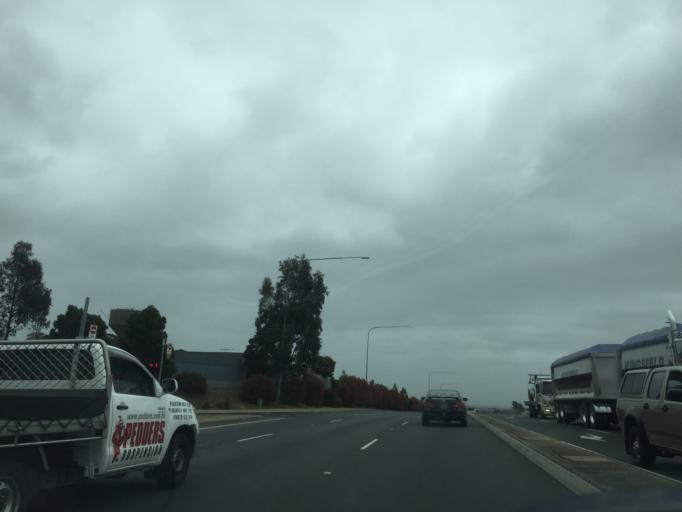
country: AU
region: New South Wales
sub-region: Blacktown
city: Stanhope Gardens
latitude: -33.7382
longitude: 150.9180
